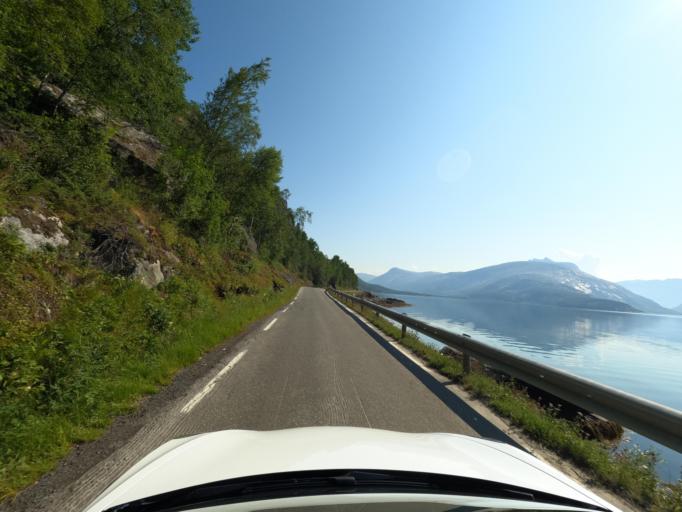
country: NO
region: Nordland
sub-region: Narvik
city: Narvik
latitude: 68.2881
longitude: 17.3669
